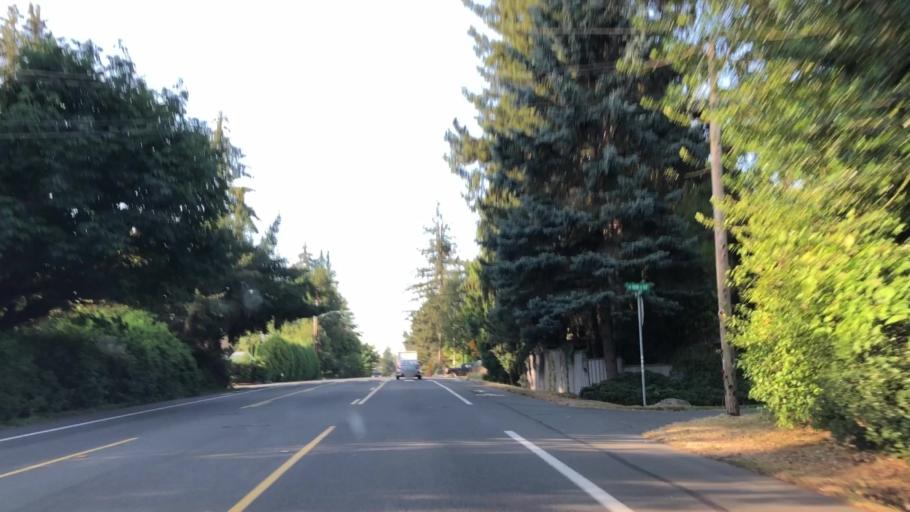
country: US
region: Washington
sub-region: King County
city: Kingsgate
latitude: 47.6970
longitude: -122.1758
